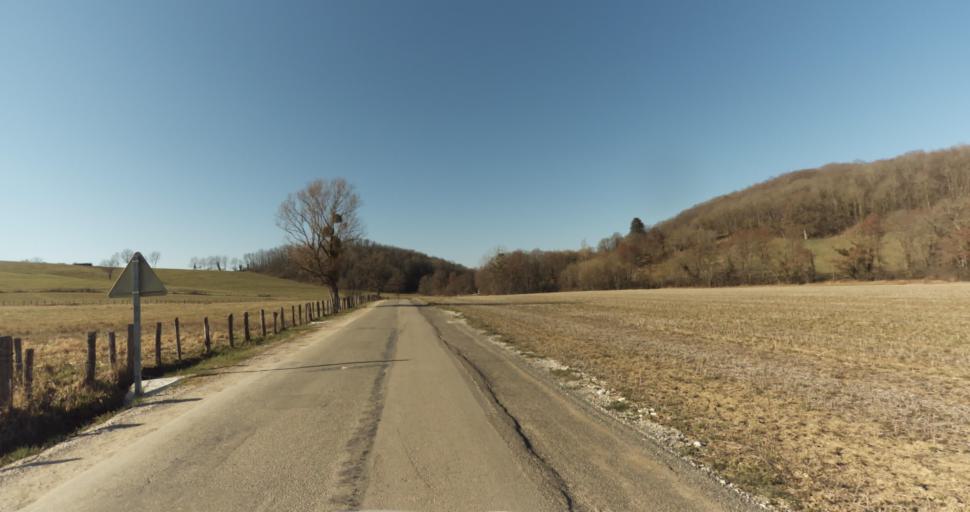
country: FR
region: Franche-Comte
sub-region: Departement du Jura
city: Montmorot
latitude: 46.7006
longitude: 5.5314
